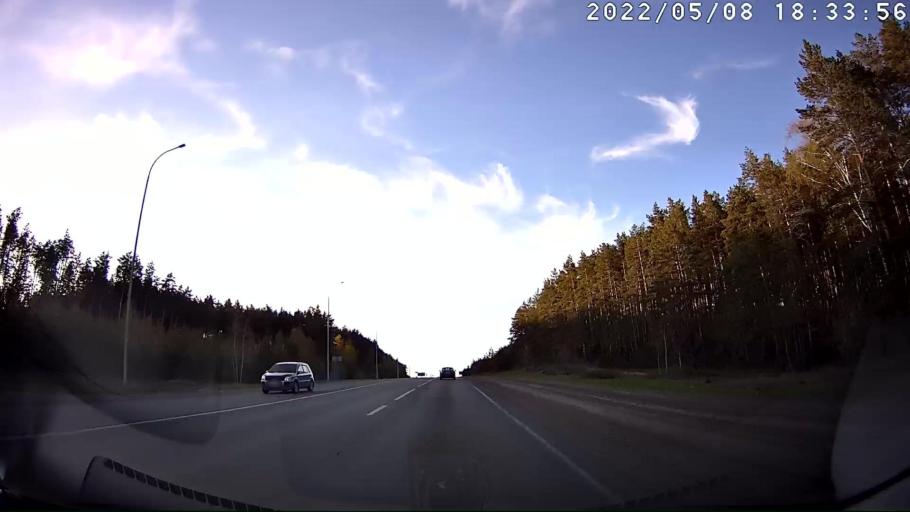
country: RU
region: Mariy-El
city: Volzhsk
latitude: 55.8952
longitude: 48.3565
